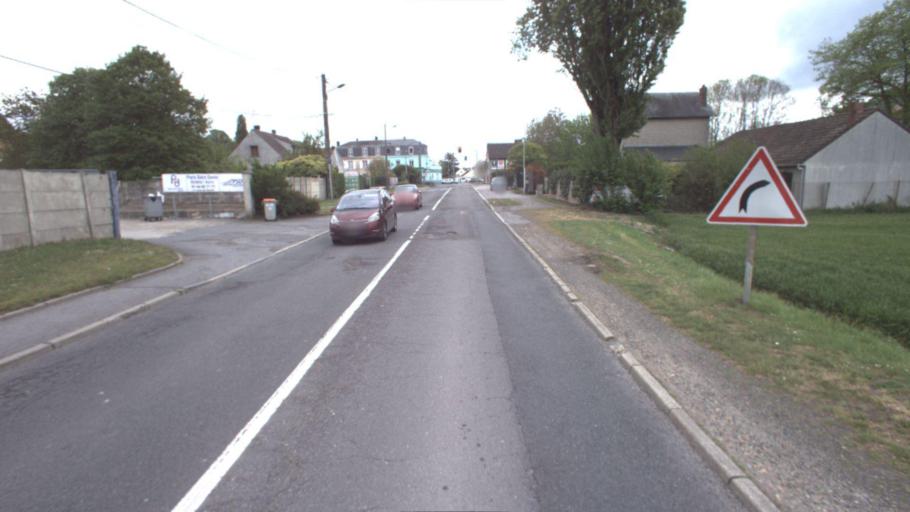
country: FR
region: Picardie
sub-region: Departement de l'Oise
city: Lagny-le-Sec
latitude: 49.0923
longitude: 2.7498
